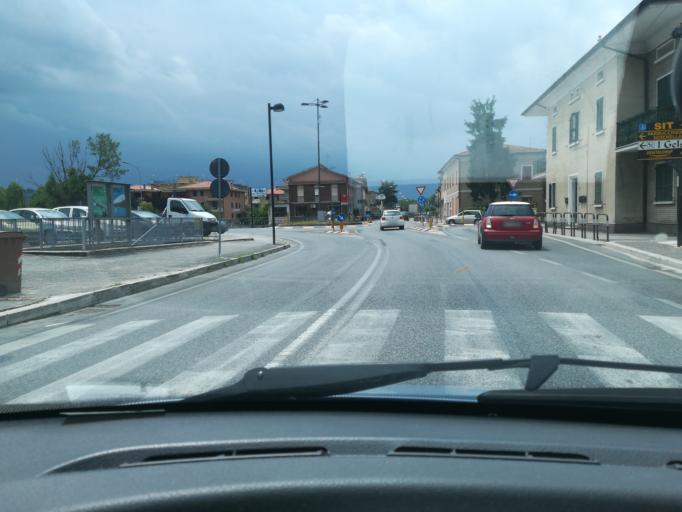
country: IT
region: The Marches
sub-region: Provincia di Macerata
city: Montecassiano
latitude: 43.3556
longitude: 13.4787
